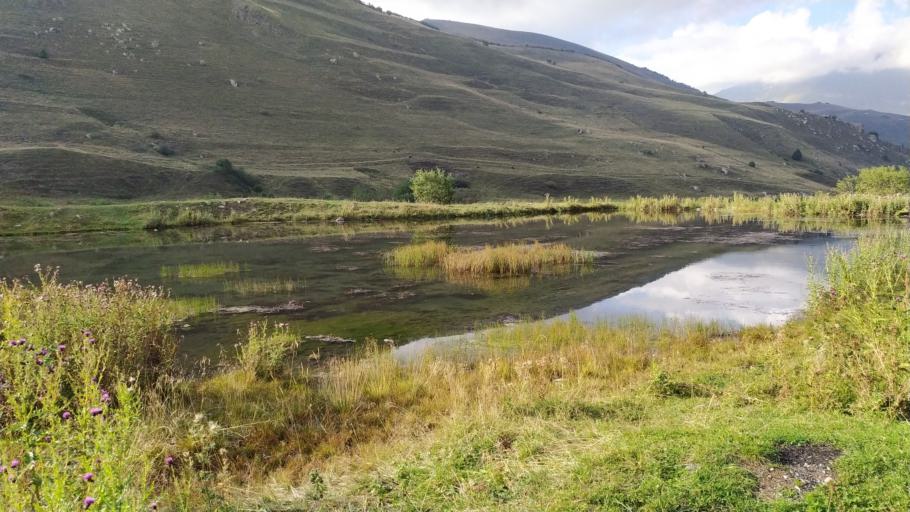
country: RU
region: North Ossetia
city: Verkhniy Fiagdon
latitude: 42.7988
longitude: 44.3752
